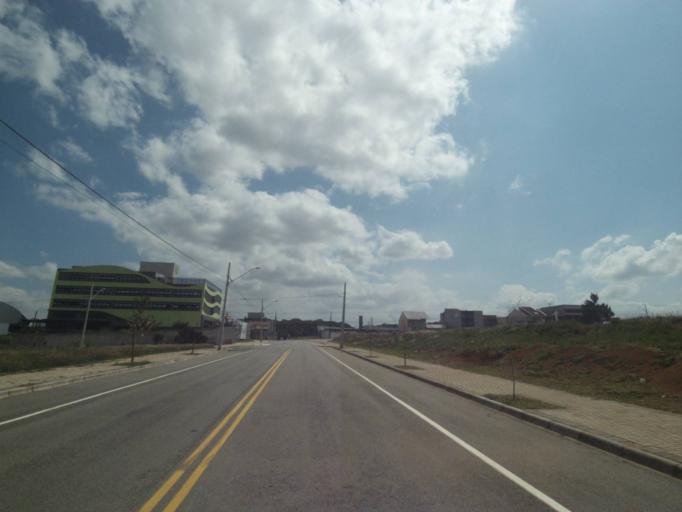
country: BR
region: Parana
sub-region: Curitiba
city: Curitiba
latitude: -25.5080
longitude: -49.3088
